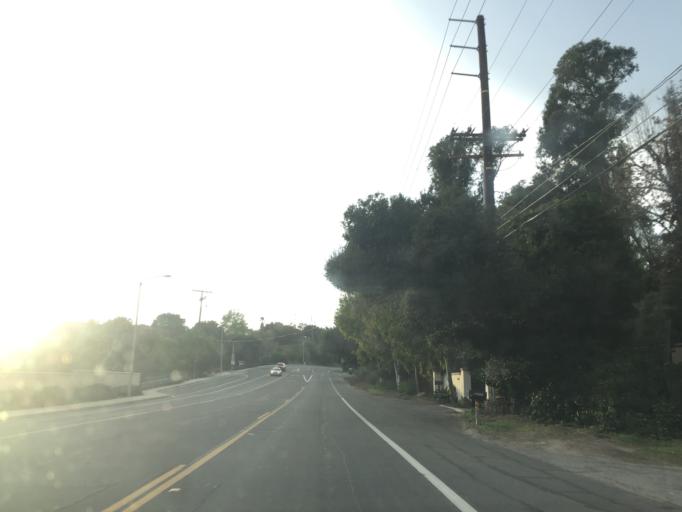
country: US
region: California
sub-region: Santa Barbara County
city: Goleta
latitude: 34.4516
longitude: -119.8018
